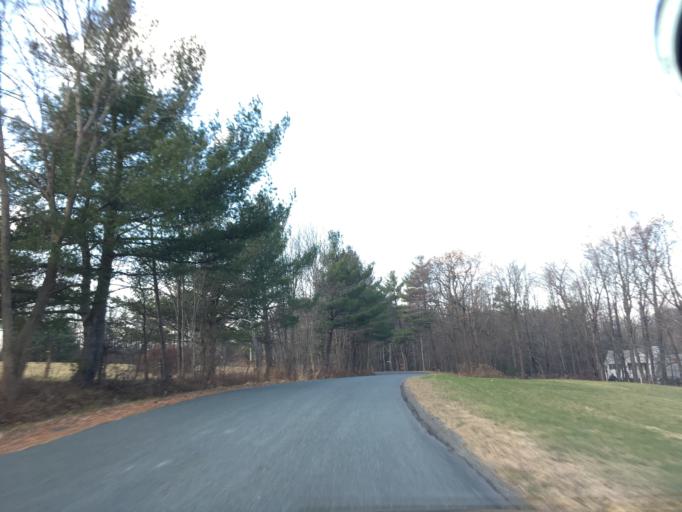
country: US
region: New York
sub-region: Rensselaer County
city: West Sand Lake
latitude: 42.6153
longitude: -73.6209
